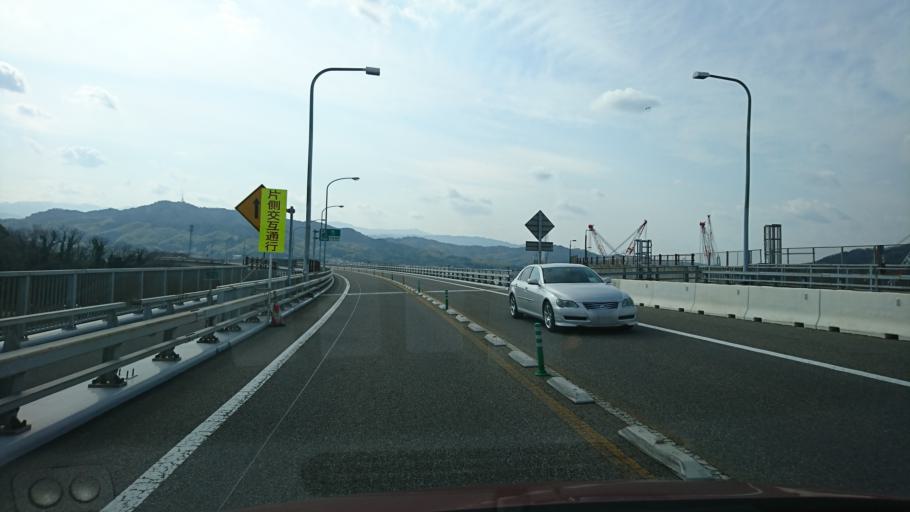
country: JP
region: Hiroshima
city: Takehara
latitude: 34.1115
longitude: 132.9772
